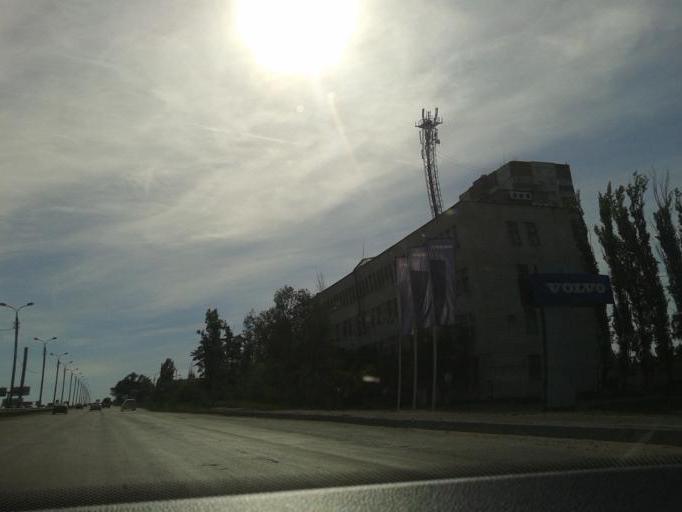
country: RU
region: Volgograd
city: Volgograd
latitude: 48.7564
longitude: 44.4902
